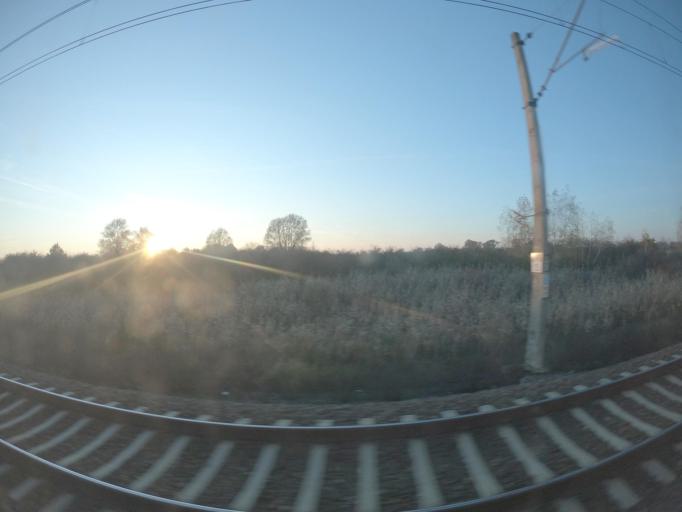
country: PL
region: Lubusz
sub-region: Powiat slubicki
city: Gorzyca
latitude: 52.5385
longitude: 14.6508
